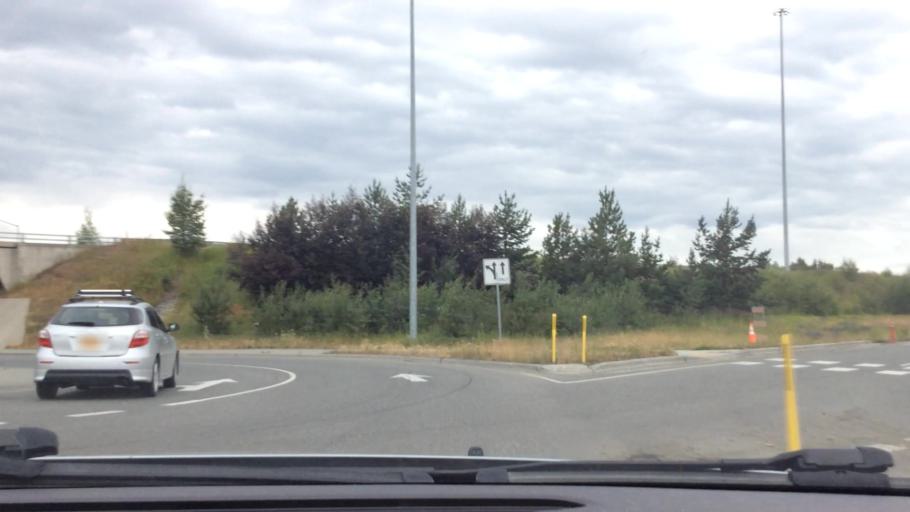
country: US
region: Alaska
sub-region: Anchorage Municipality
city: Anchorage
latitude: 61.1665
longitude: -149.8550
